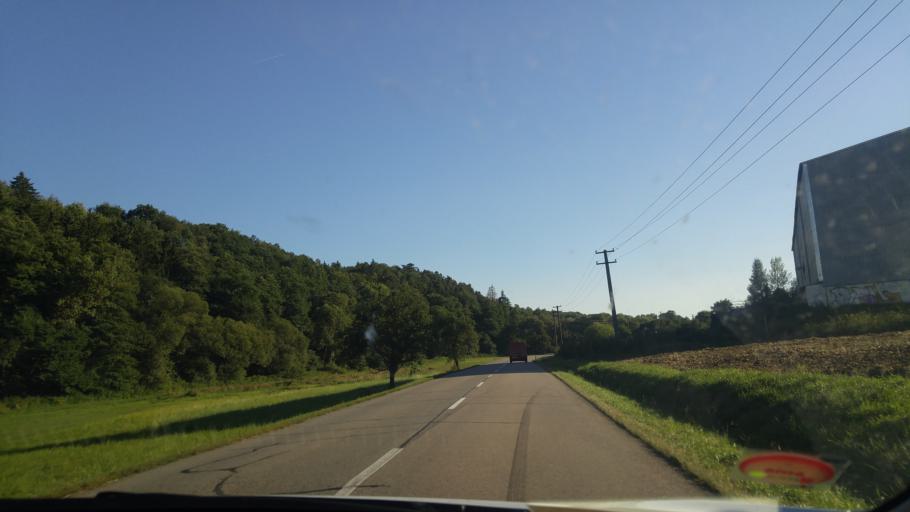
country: CZ
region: South Moravian
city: Veverska Bityska
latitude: 49.2476
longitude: 16.4476
